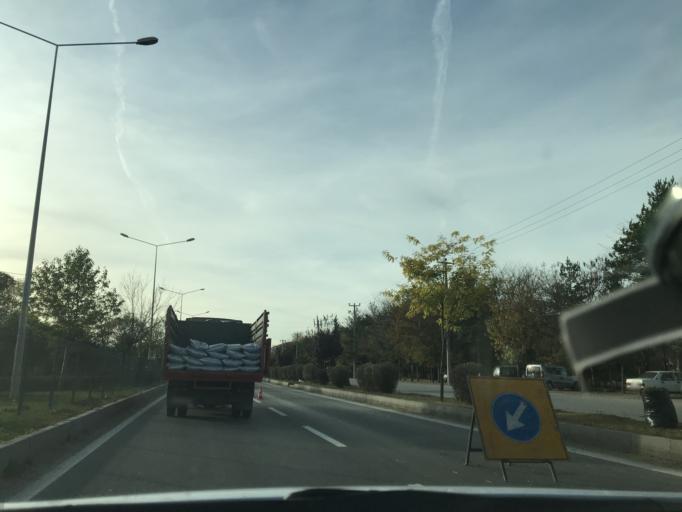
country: TR
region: Bolu
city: Bolu
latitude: 40.7377
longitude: 31.6177
